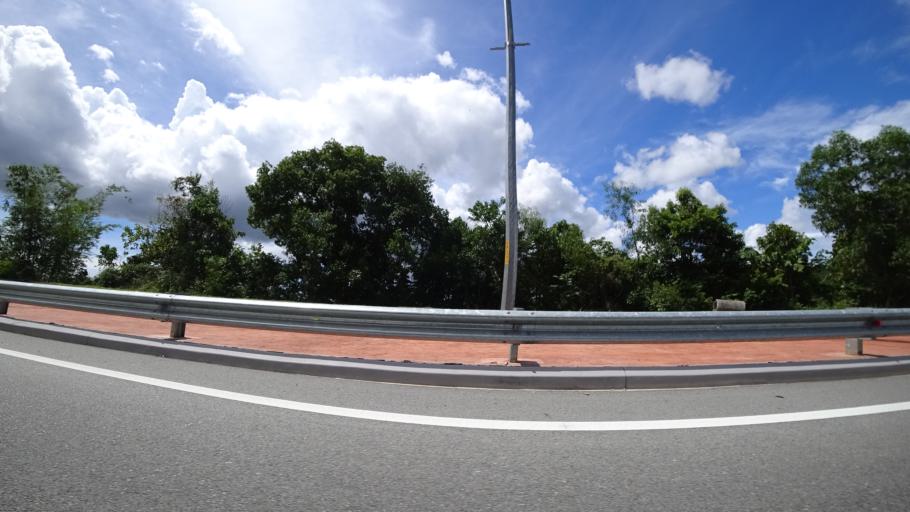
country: BN
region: Brunei and Muara
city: Bandar Seri Begawan
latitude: 4.8787
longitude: 114.9452
